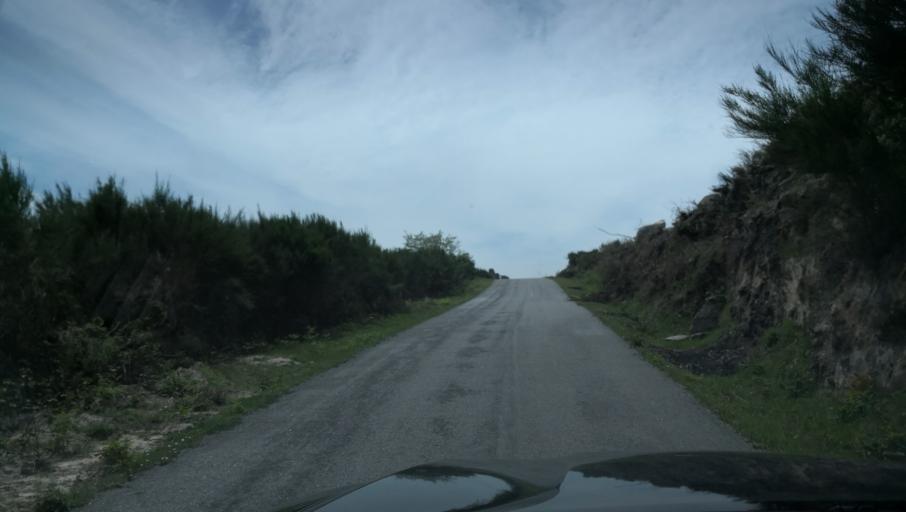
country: PT
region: Vila Real
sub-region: Vila Real
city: Vila Real
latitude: 41.3003
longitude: -7.8120
